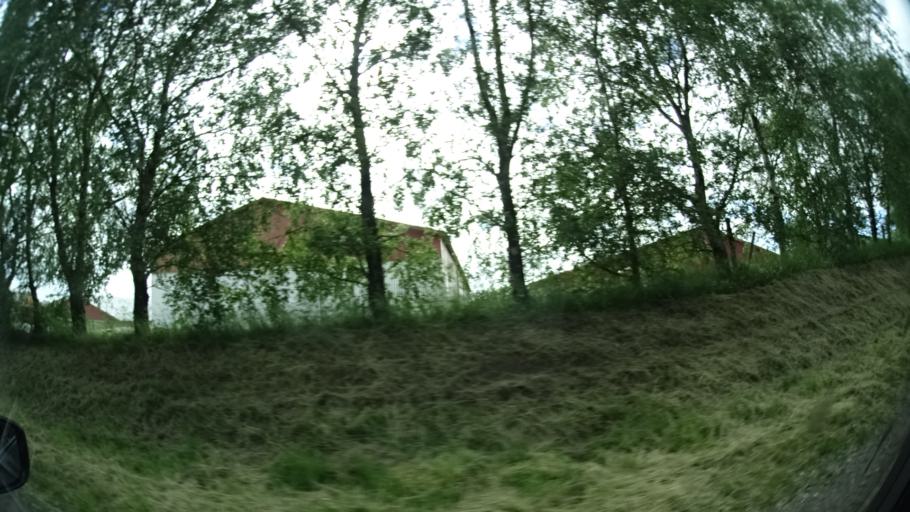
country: DK
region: Central Jutland
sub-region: Norddjurs Kommune
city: Grenaa
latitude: 56.4546
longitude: 10.7122
